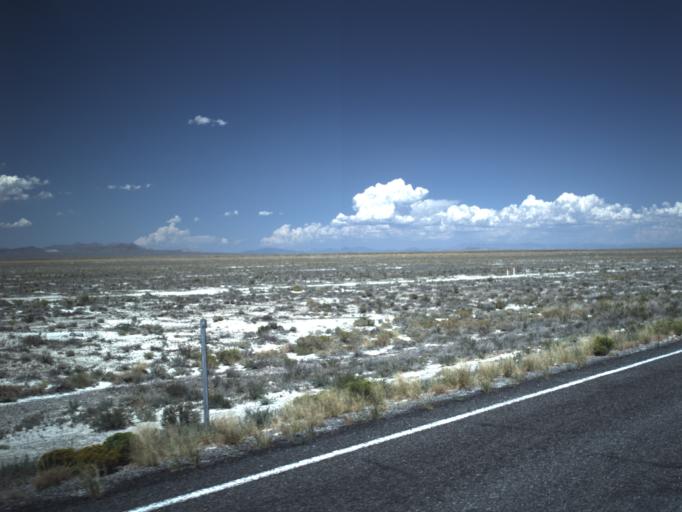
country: US
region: Utah
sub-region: Millard County
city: Delta
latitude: 39.1953
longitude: -112.9921
